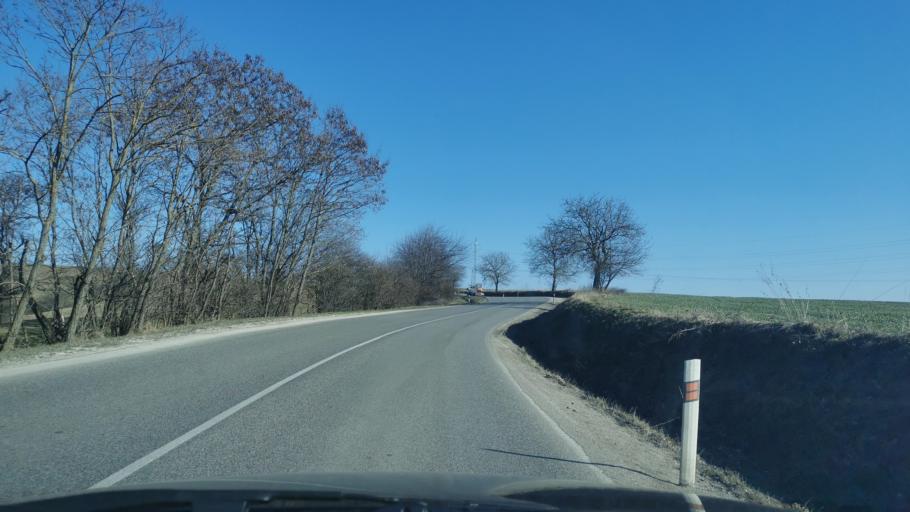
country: SK
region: Trnavsky
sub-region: Okres Senica
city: Senica
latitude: 48.7324
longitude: 17.4156
